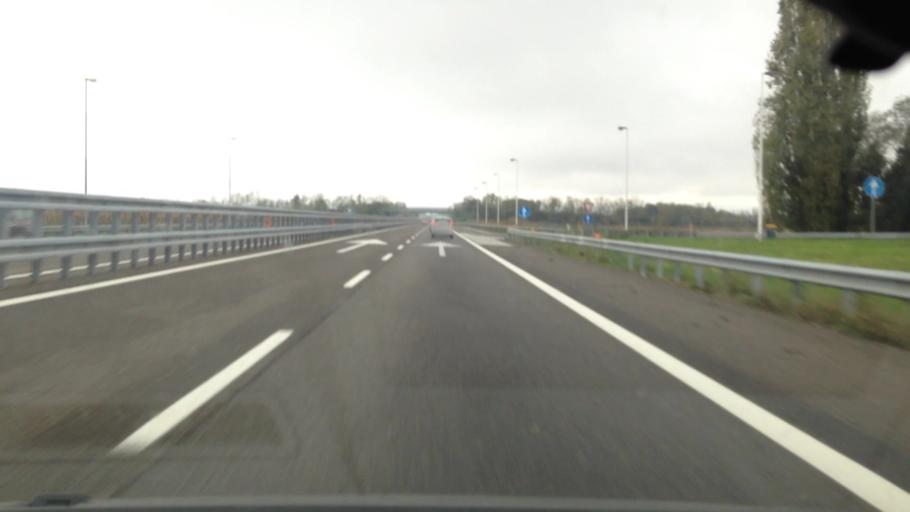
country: IT
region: Piedmont
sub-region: Provincia di Asti
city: Villanova d'Asti
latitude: 44.9504
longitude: 7.9490
